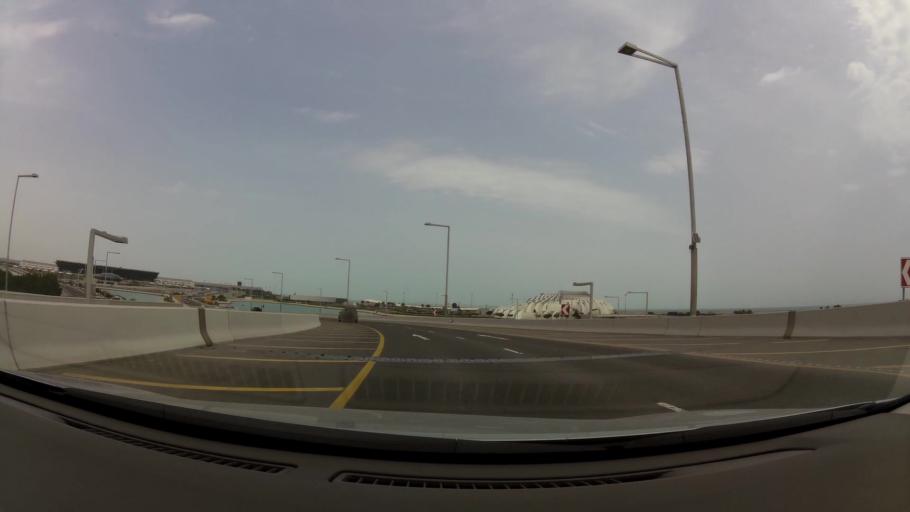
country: QA
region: Al Wakrah
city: Al Wakrah
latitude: 25.2513
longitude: 51.6172
